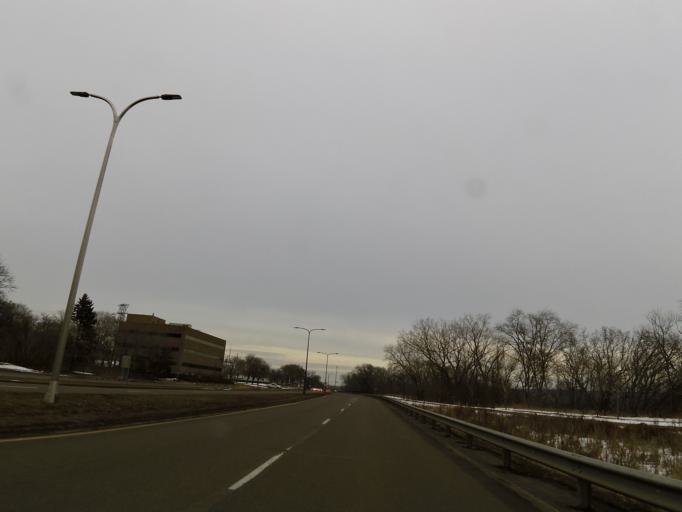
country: US
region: Minnesota
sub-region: Dakota County
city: Mendota Heights
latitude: 44.9024
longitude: -93.1587
